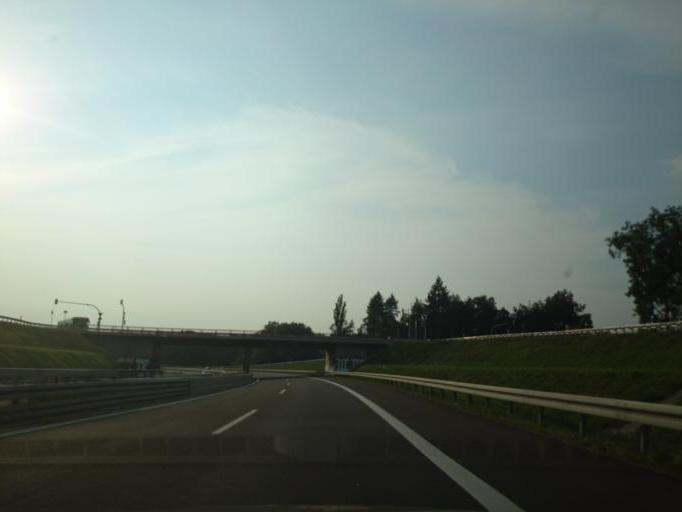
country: DE
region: Berlin
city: Wannsee
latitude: 52.3744
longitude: 13.1696
